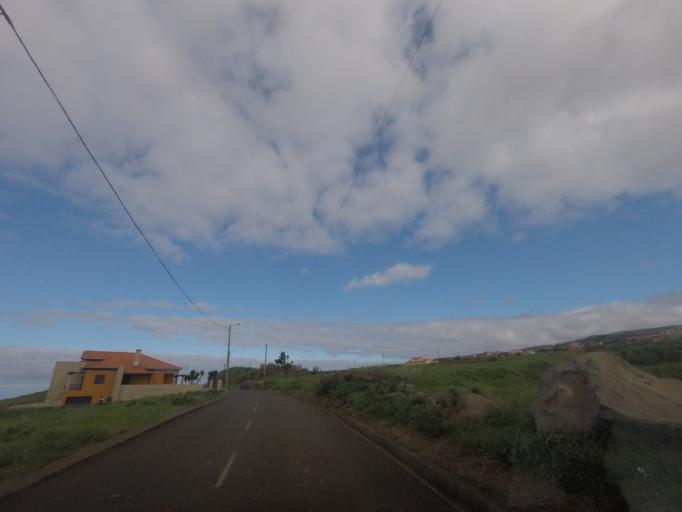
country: PT
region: Madeira
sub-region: Calheta
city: Faja da Ovelha
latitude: 32.8100
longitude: -17.2563
